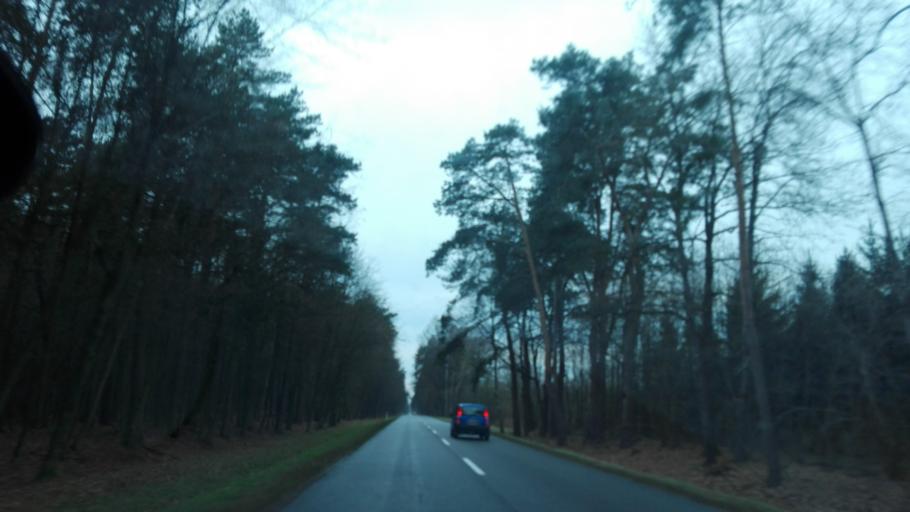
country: PL
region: Lublin Voivodeship
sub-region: Powiat radzynski
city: Komarowka Podlaska
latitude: 51.7772
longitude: 22.8859
